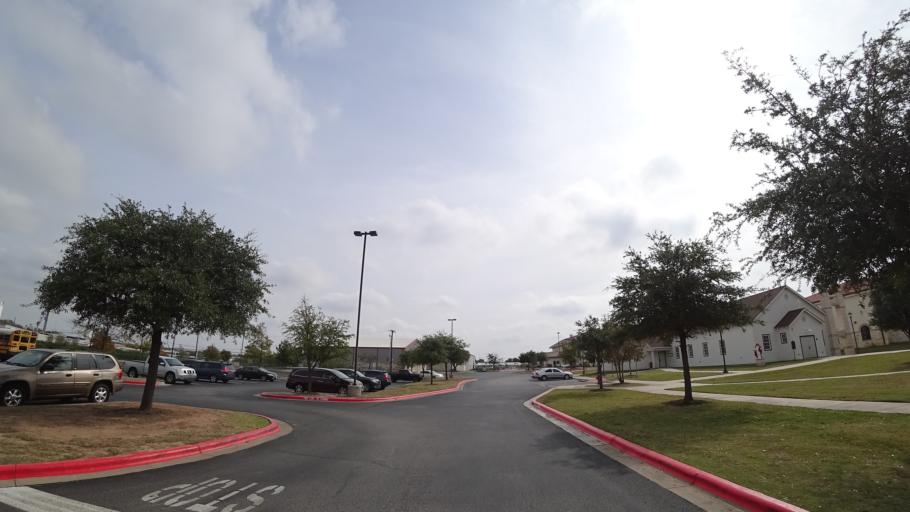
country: US
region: Texas
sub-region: Williamson County
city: Round Rock
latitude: 30.5017
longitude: -97.6877
